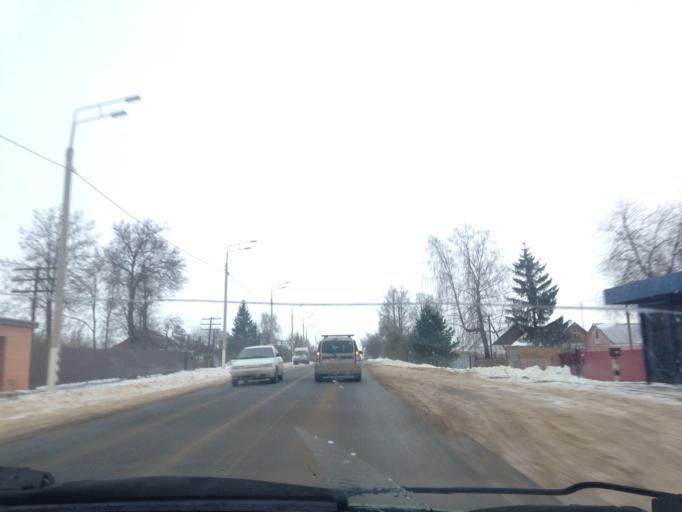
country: RU
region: Tula
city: Shchekino
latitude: 53.9901
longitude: 37.5058
